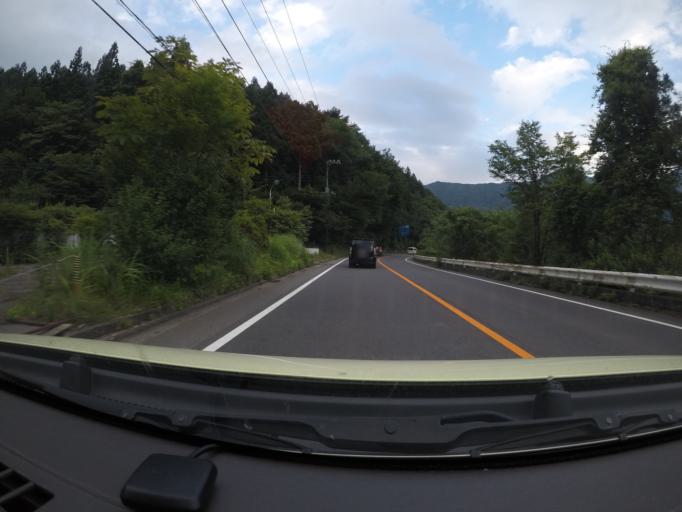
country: JP
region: Tochigi
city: Nikko
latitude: 36.7352
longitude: 139.5463
